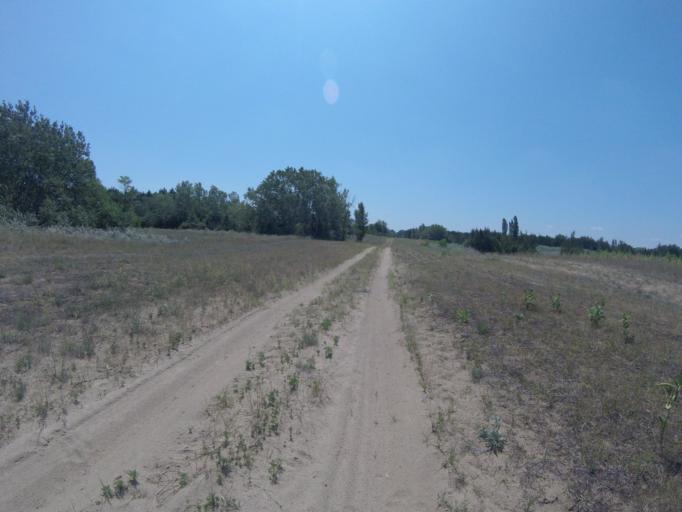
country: HU
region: Bacs-Kiskun
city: Jaszszentlaszlo
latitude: 46.6145
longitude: 19.7109
